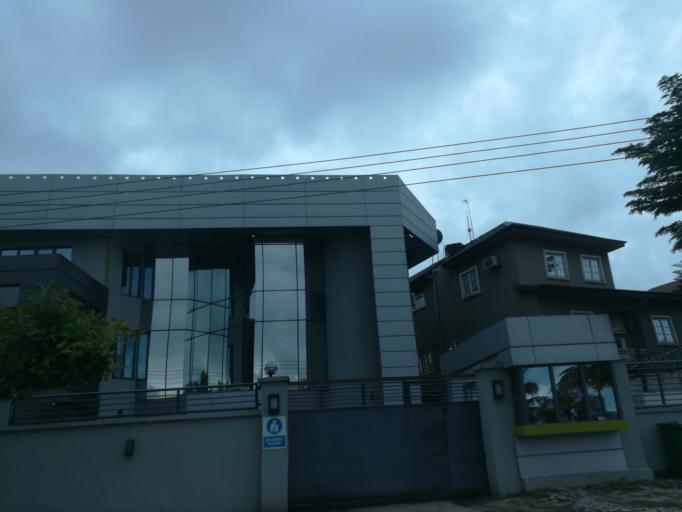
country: NG
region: Lagos
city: Ikoyi
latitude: 6.4450
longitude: 3.4542
